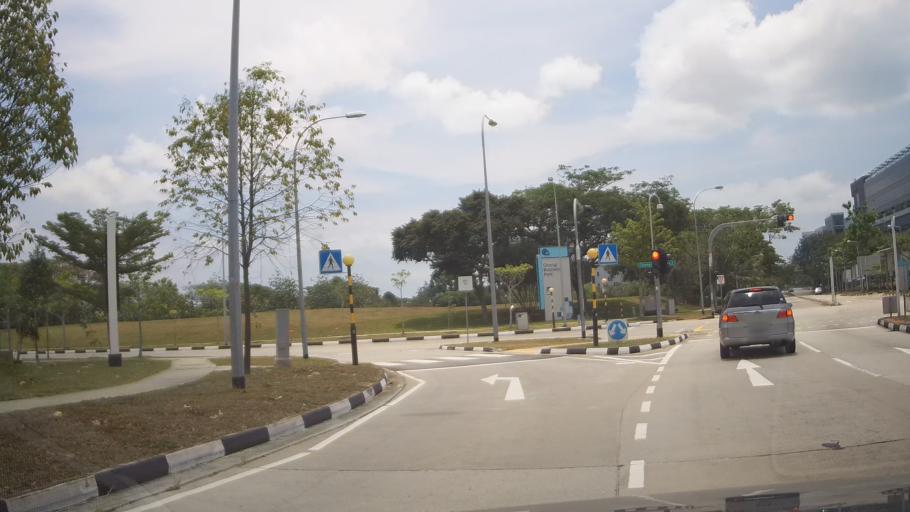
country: SG
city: Singapore
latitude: 1.3396
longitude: 103.9646
